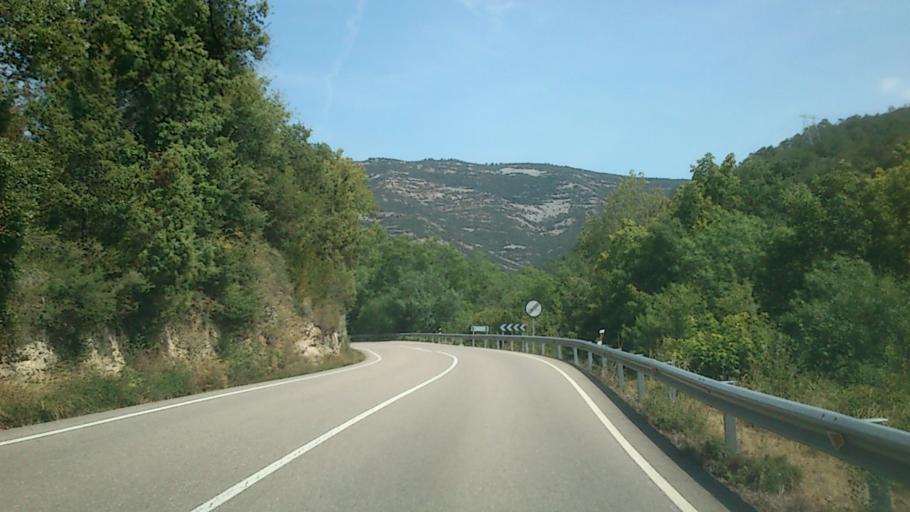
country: ES
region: Castille and Leon
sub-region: Provincia de Burgos
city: Trespaderne
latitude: 42.8760
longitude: -3.3301
